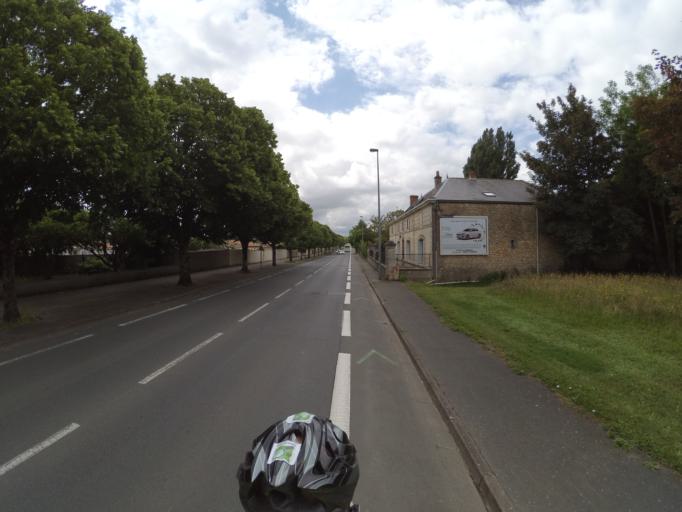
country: FR
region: Poitou-Charentes
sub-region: Departement de la Charente-Maritime
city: Rochefort
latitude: 45.9576
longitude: -0.9693
